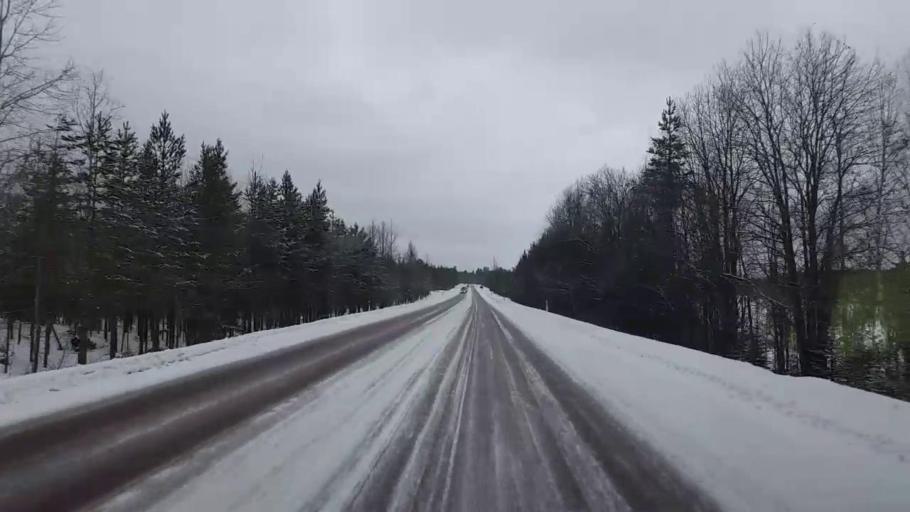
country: SE
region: Jaemtland
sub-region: Bergs Kommun
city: Hoverberg
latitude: 62.4502
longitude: 14.5611
